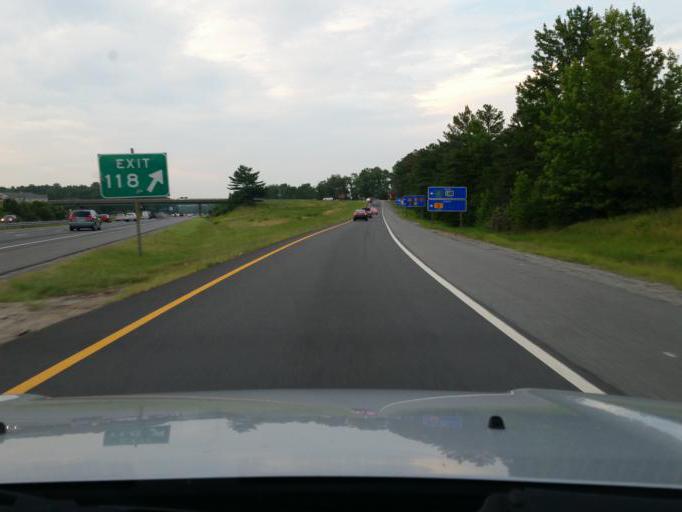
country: US
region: Virginia
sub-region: Spotsylvania County
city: Spotsylvania Courthouse
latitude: 38.1295
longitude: -77.5123
